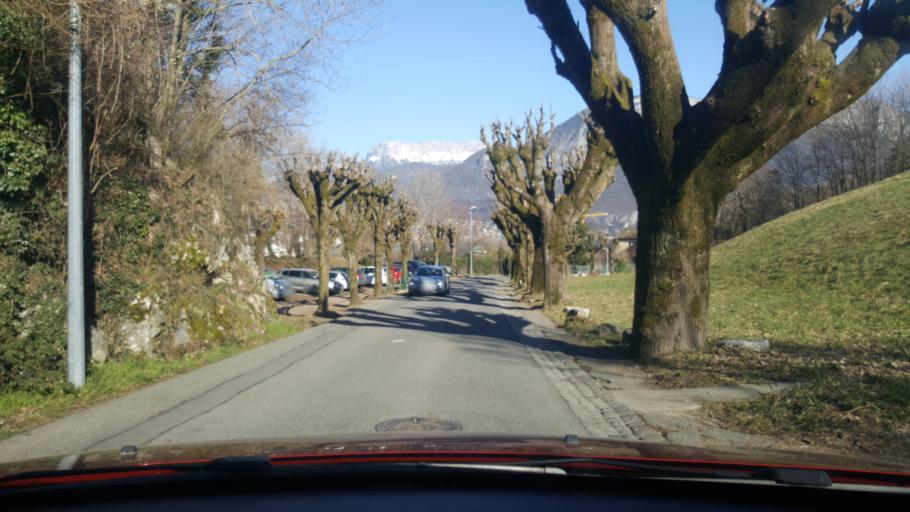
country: FR
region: Rhone-Alpes
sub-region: Departement de la Haute-Savoie
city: Annecy
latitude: 45.8930
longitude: 6.1257
